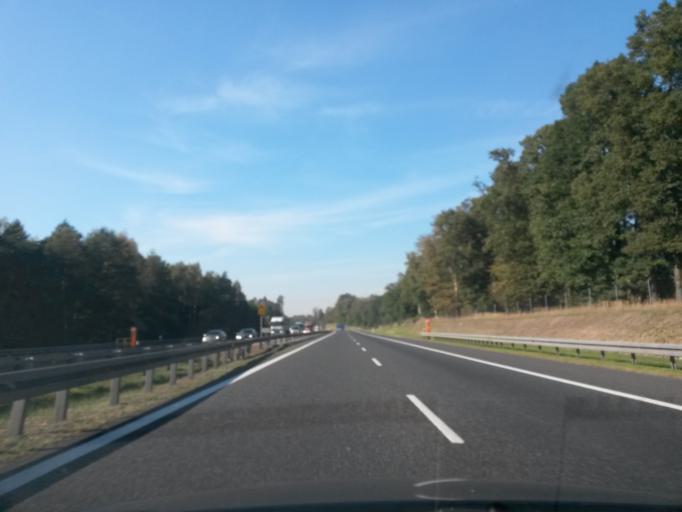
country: PL
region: Opole Voivodeship
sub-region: Powiat strzelecki
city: Ujazd
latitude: 50.4380
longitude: 18.3633
